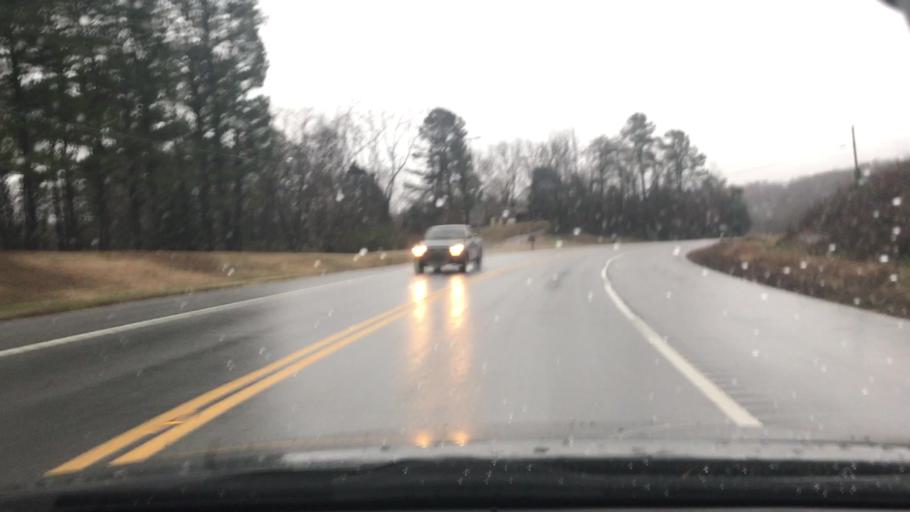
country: US
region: Tennessee
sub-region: Cheatham County
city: Ashland City
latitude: 36.2879
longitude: -87.1478
